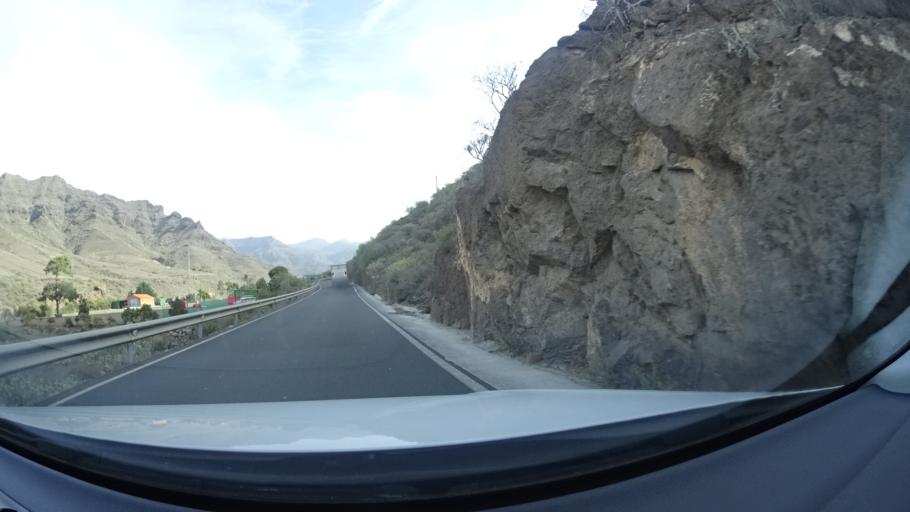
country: ES
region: Canary Islands
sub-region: Provincia de Las Palmas
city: Mogan
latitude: 27.8687
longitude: -15.7397
